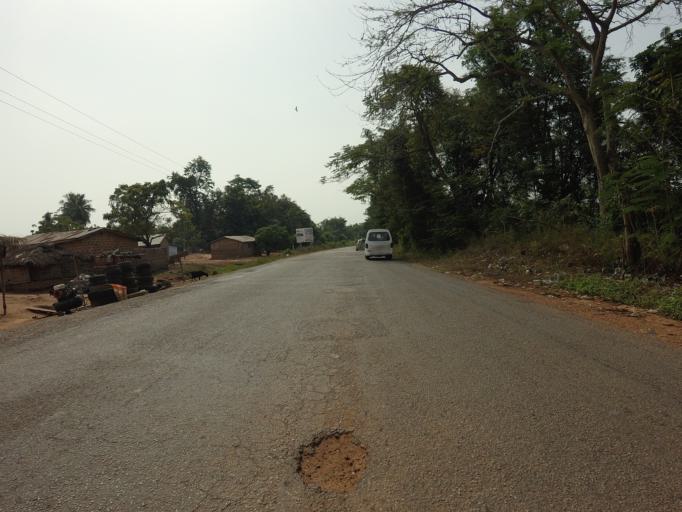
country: GH
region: Volta
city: Ho
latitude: 6.3765
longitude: 0.1885
